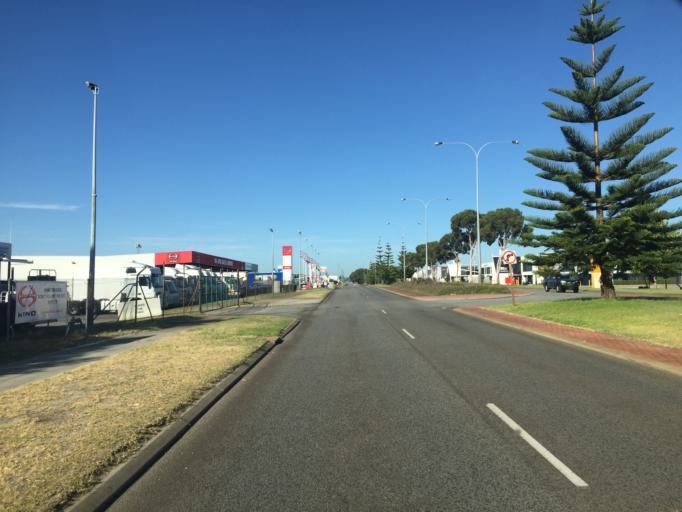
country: AU
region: Western Australia
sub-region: Canning
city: Queens Park
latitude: -31.9908
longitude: 115.9464
